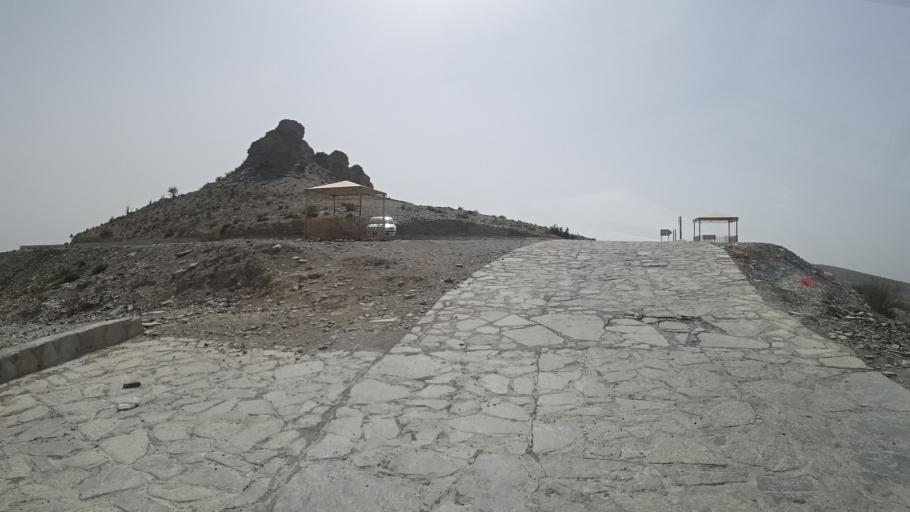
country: OM
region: Al Batinah
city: Bayt al `Awabi
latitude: 23.1674
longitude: 57.4148
